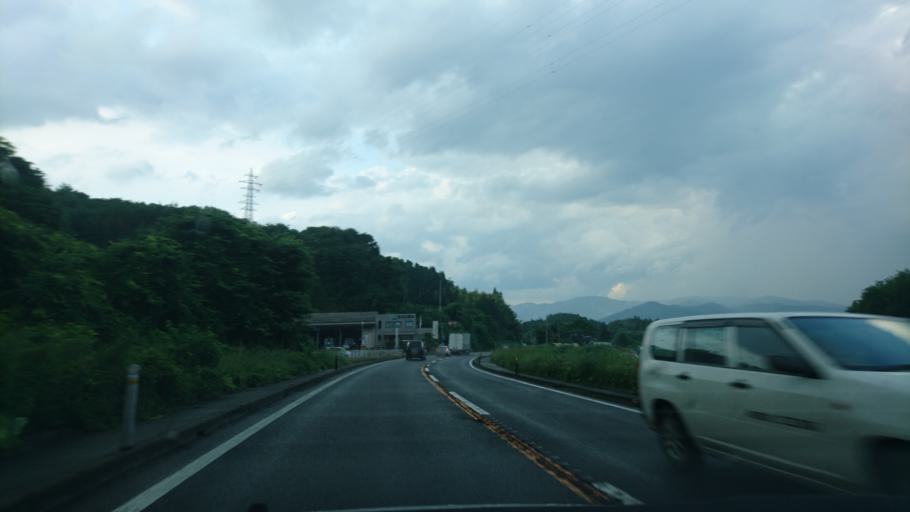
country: JP
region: Iwate
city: Ichinoseki
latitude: 38.9485
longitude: 141.1184
